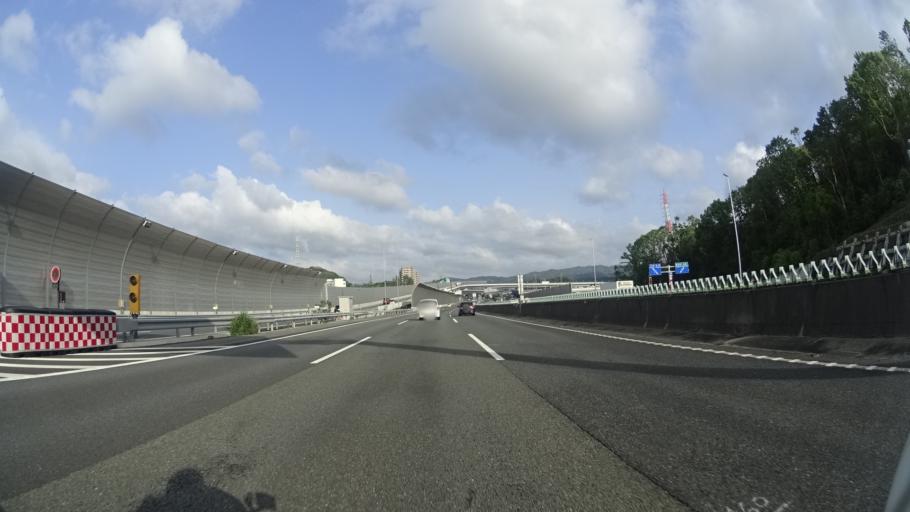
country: JP
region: Osaka
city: Takatsuki
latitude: 34.8641
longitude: 135.6322
